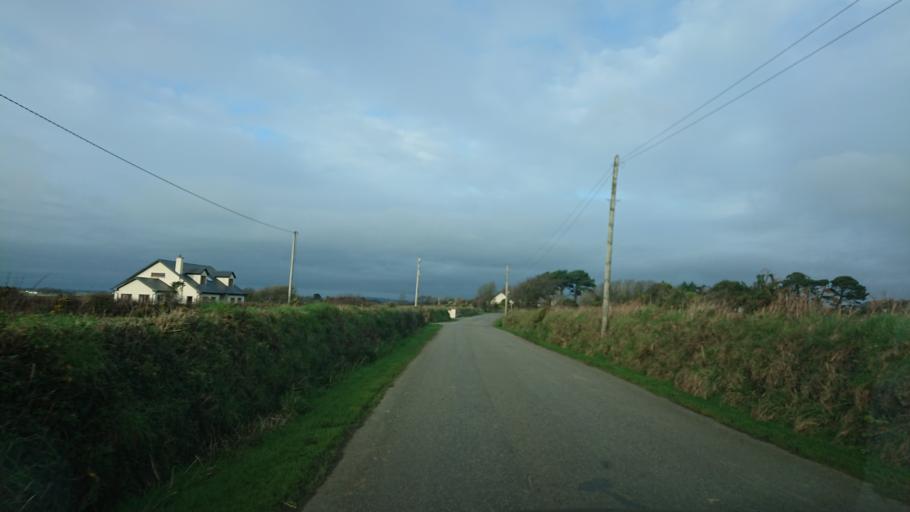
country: IE
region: Munster
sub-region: Waterford
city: Tra Mhor
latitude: 52.1539
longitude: -7.2147
